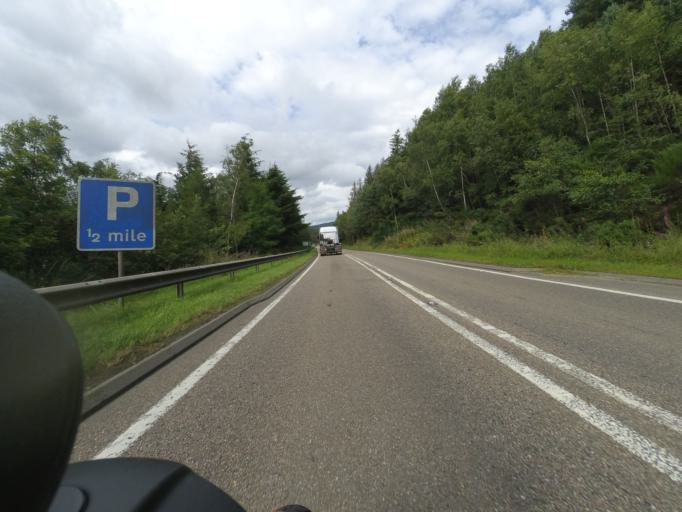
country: GB
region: Scotland
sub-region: Moray
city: Rothes
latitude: 57.4850
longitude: -3.1941
